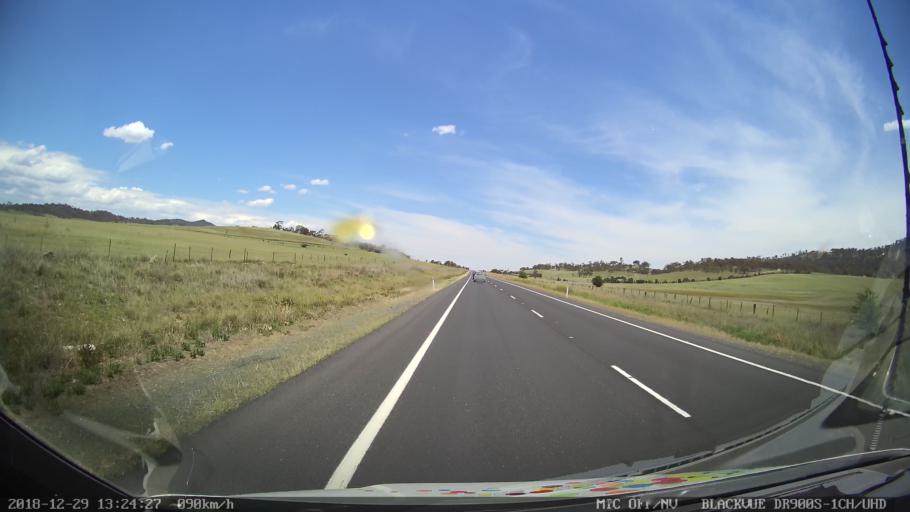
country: AU
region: New South Wales
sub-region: Cooma-Monaro
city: Cooma
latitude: -35.8297
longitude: 149.1625
